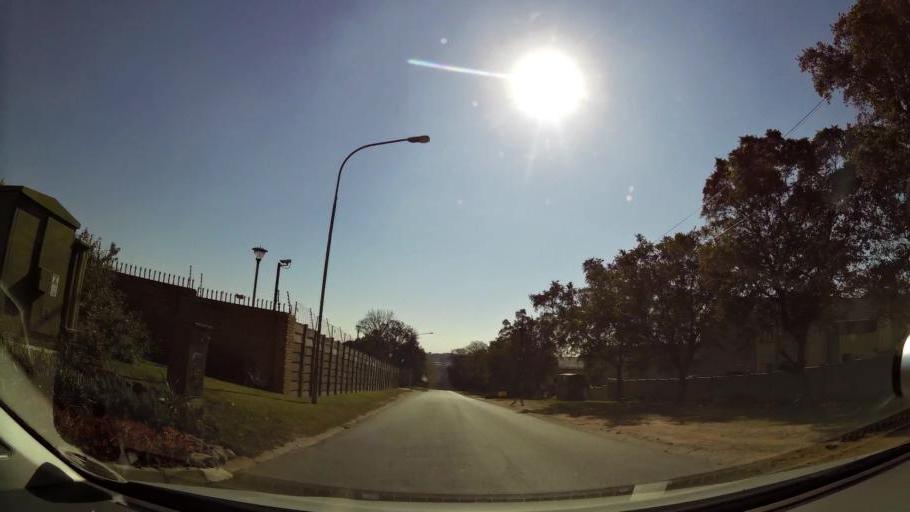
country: ZA
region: Gauteng
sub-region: City of Johannesburg Metropolitan Municipality
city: Modderfontein
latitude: -26.1251
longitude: 28.1045
